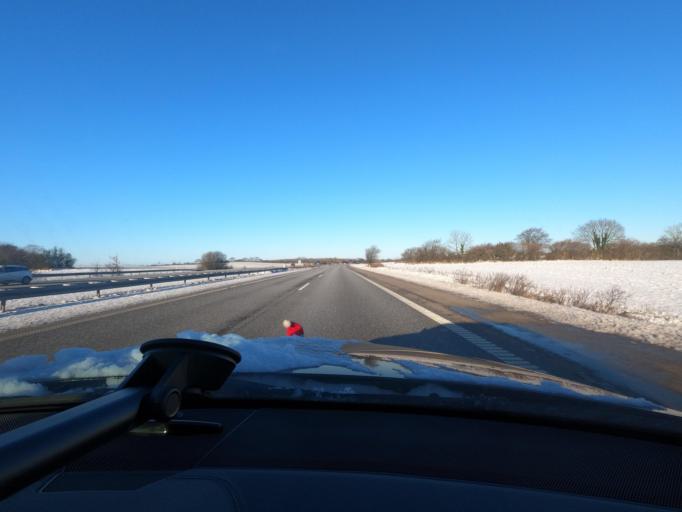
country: DK
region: South Denmark
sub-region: Aabenraa Kommune
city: Rodekro
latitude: 55.0326
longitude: 9.3564
